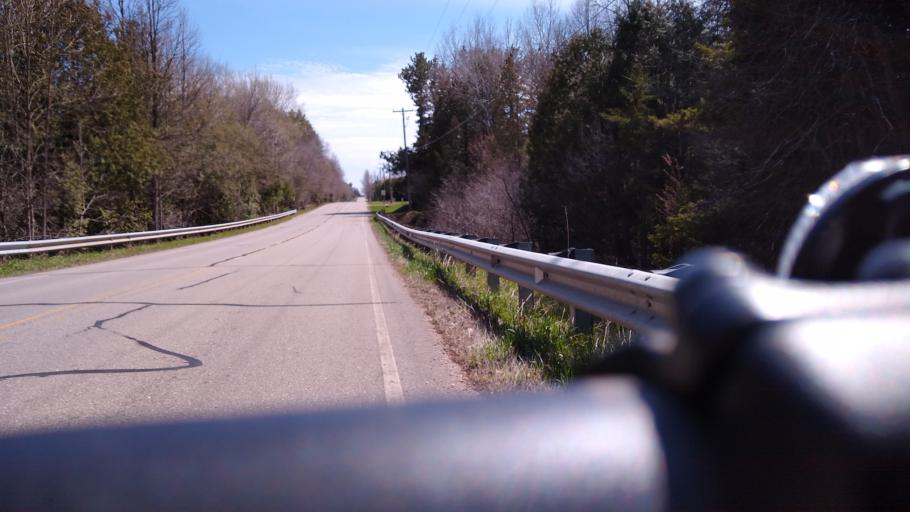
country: US
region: Michigan
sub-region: Delta County
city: Escanaba
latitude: 45.7294
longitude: -87.2025
